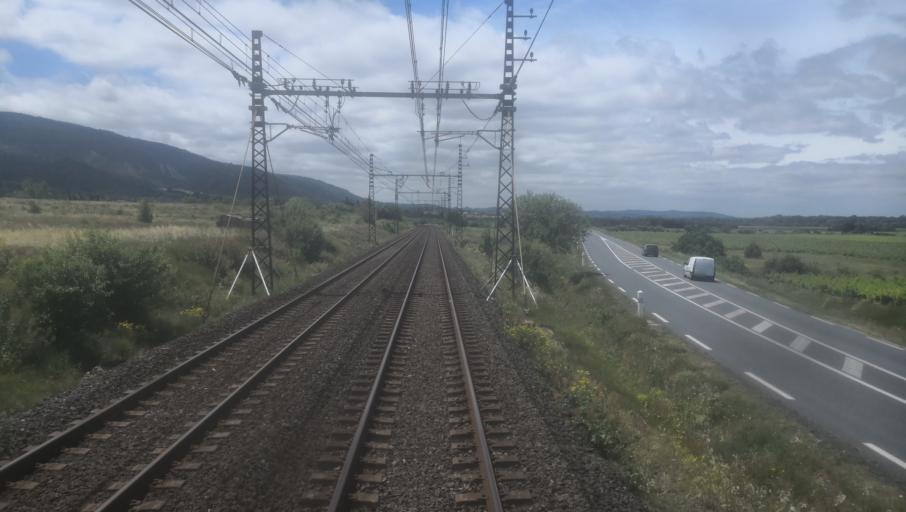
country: FR
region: Languedoc-Roussillon
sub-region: Departement de l'Aude
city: Capendu
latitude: 43.1867
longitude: 2.5406
